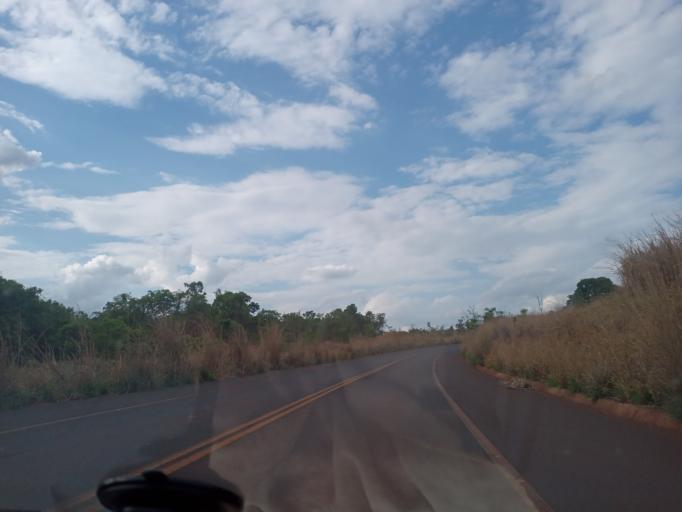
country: BR
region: Minas Gerais
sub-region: Ituiutaba
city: Ituiutaba
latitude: -19.1163
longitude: -49.5201
